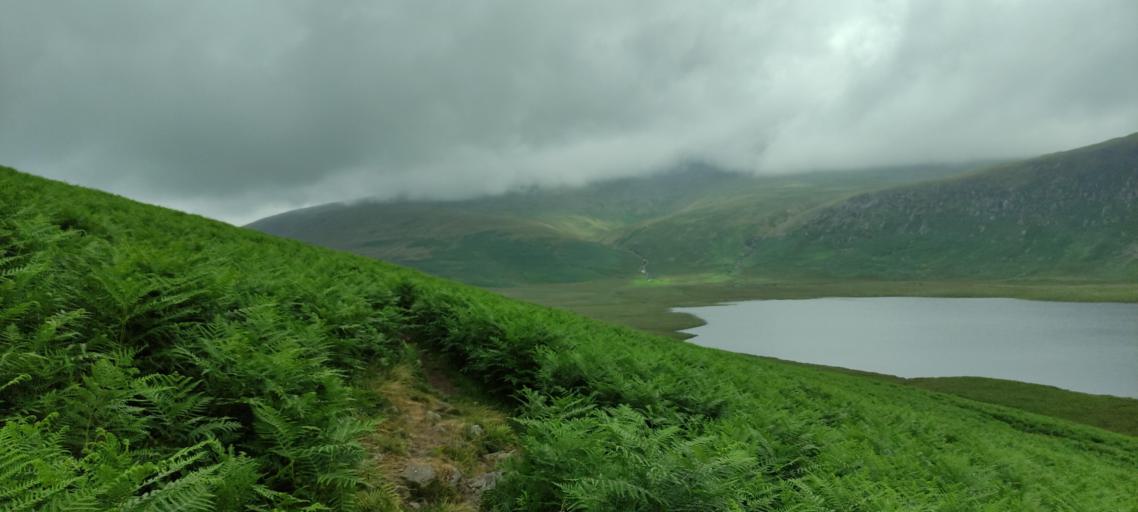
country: GB
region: England
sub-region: Cumbria
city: Seascale
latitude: 54.4268
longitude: -3.2696
